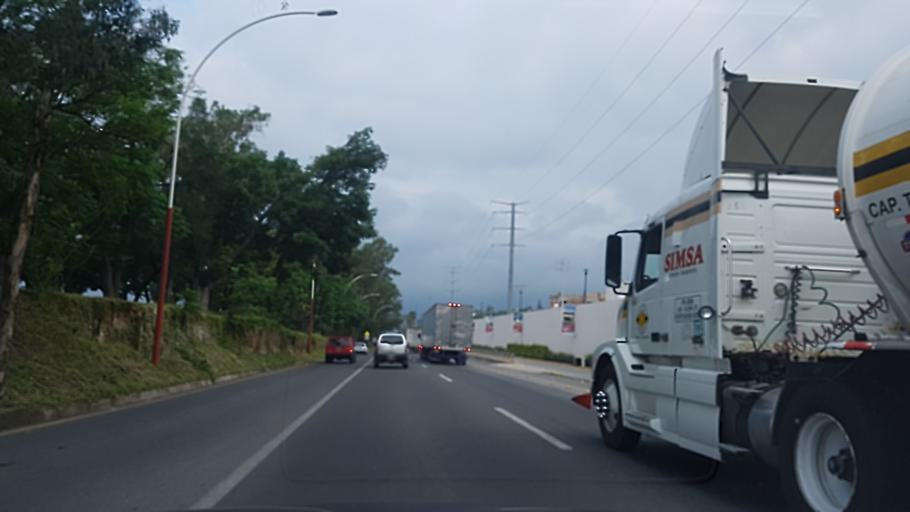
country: MX
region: Nayarit
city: Tepic
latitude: 21.4816
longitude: -104.8992
